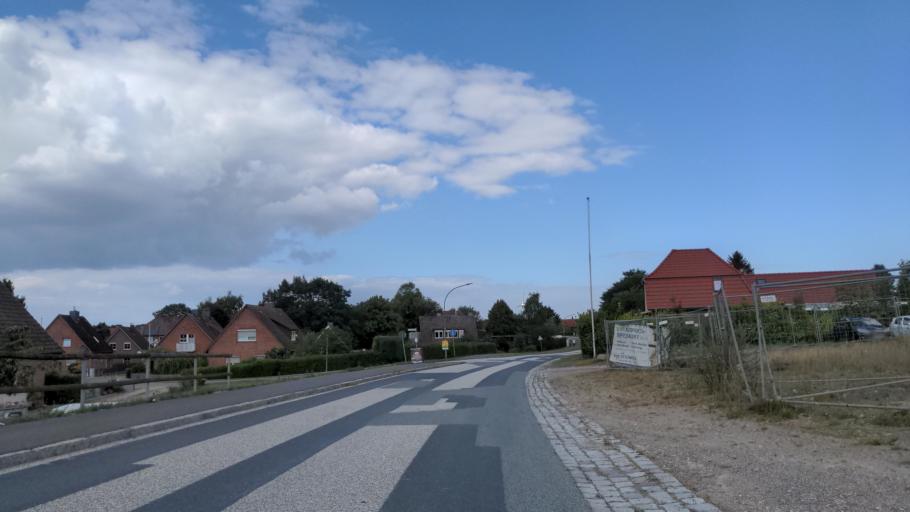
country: DE
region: Schleswig-Holstein
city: Beschendorf
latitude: 54.1805
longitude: 10.8779
